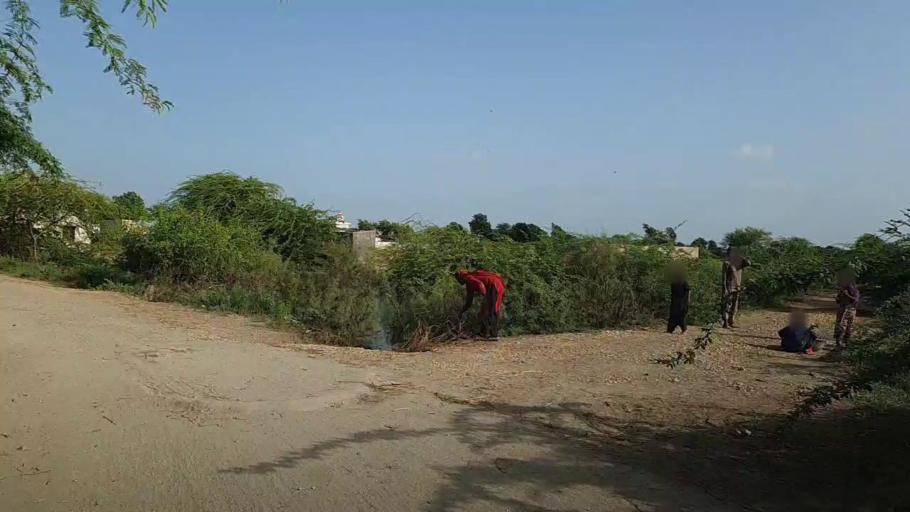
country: PK
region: Sindh
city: Kario
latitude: 24.6491
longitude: 68.4982
